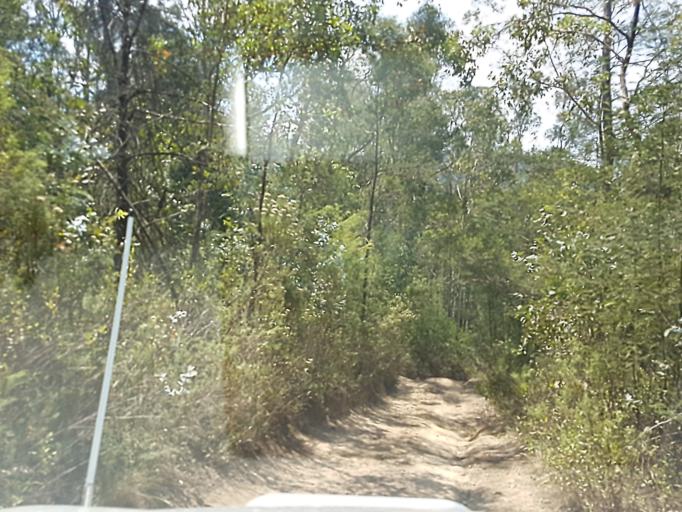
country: AU
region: Victoria
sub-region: East Gippsland
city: Lakes Entrance
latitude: -37.4029
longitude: 148.3173
